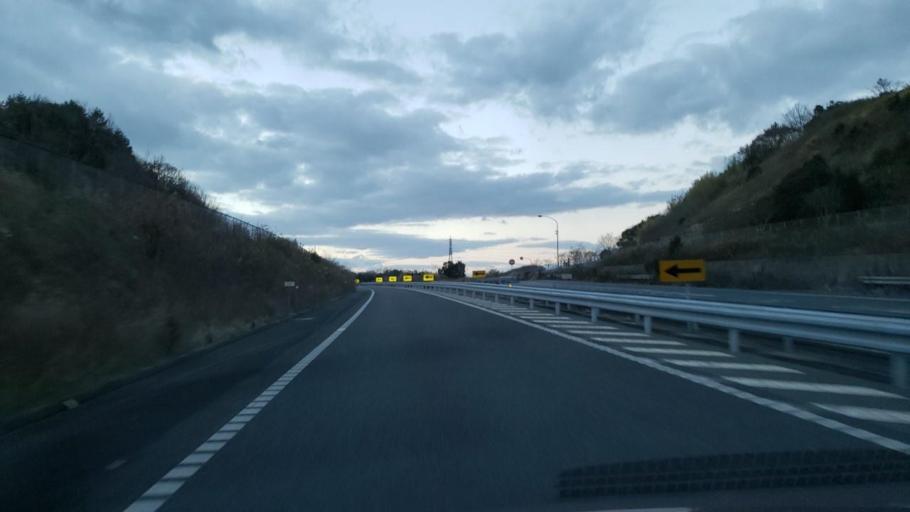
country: JP
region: Hyogo
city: Akashi
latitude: 34.6824
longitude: 135.0266
